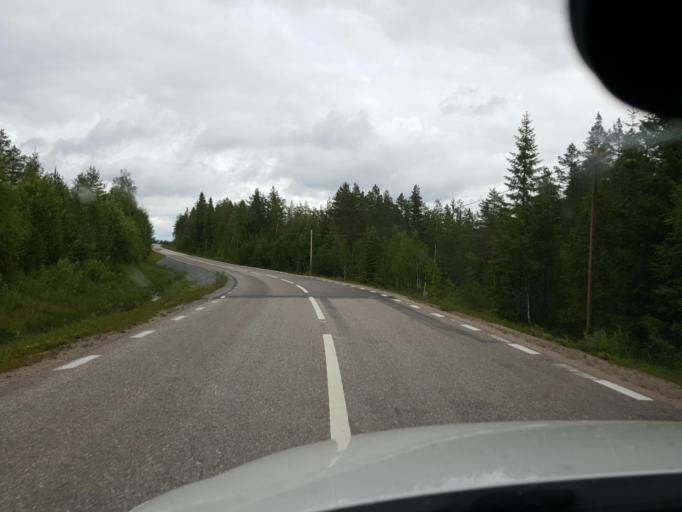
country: SE
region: Gaevleborg
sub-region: Ljusdals Kommun
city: Farila
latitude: 61.7573
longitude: 15.4731
